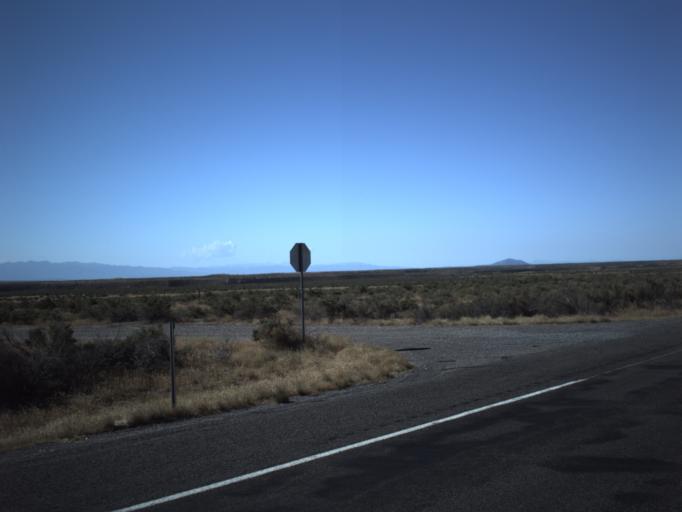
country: US
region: Utah
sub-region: Millard County
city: Delta
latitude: 39.4307
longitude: -112.4663
